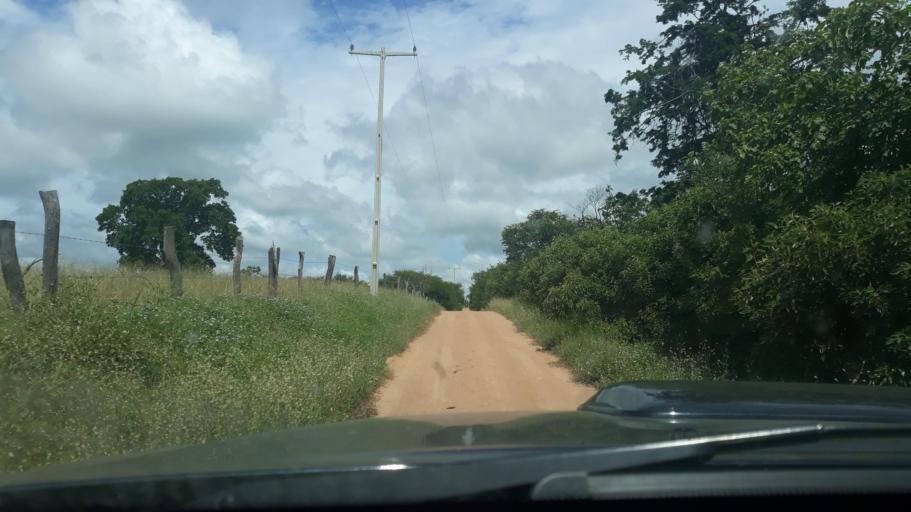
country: BR
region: Bahia
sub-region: Riacho De Santana
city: Riacho de Santana
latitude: -13.8626
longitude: -43.0253
